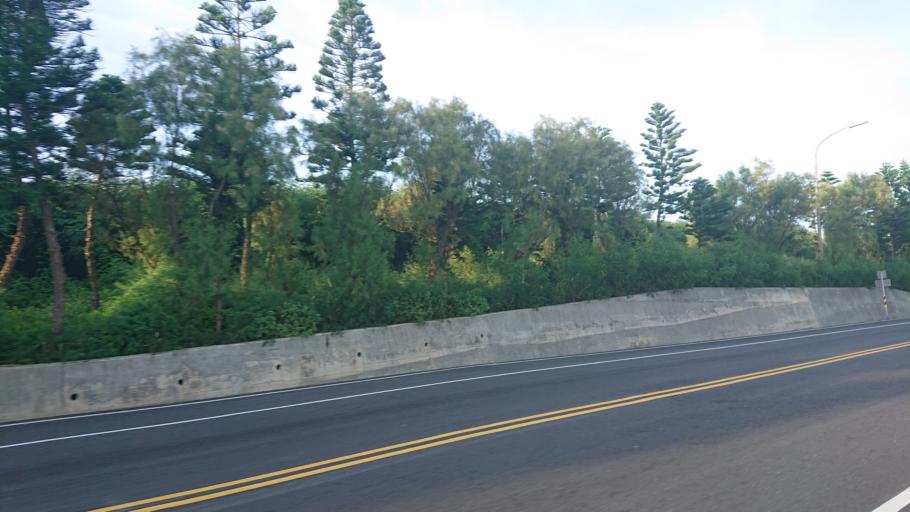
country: TW
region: Taiwan
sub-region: Penghu
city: Ma-kung
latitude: 23.6629
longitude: 119.5731
